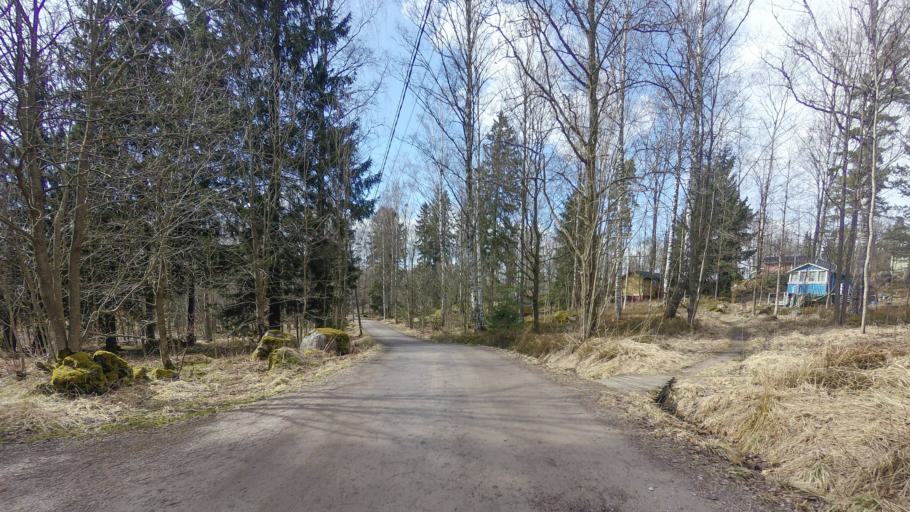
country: FI
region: Uusimaa
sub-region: Helsinki
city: Helsinki
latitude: 60.1956
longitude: 25.0102
